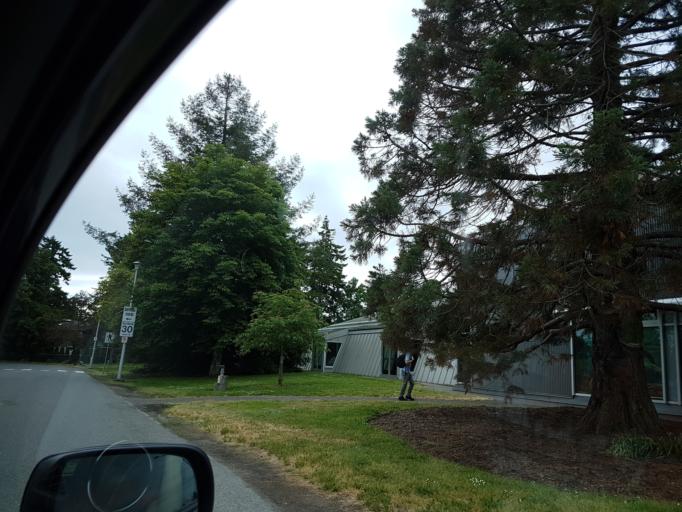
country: CA
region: British Columbia
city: Oak Bay
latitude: 48.4782
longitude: -123.3298
